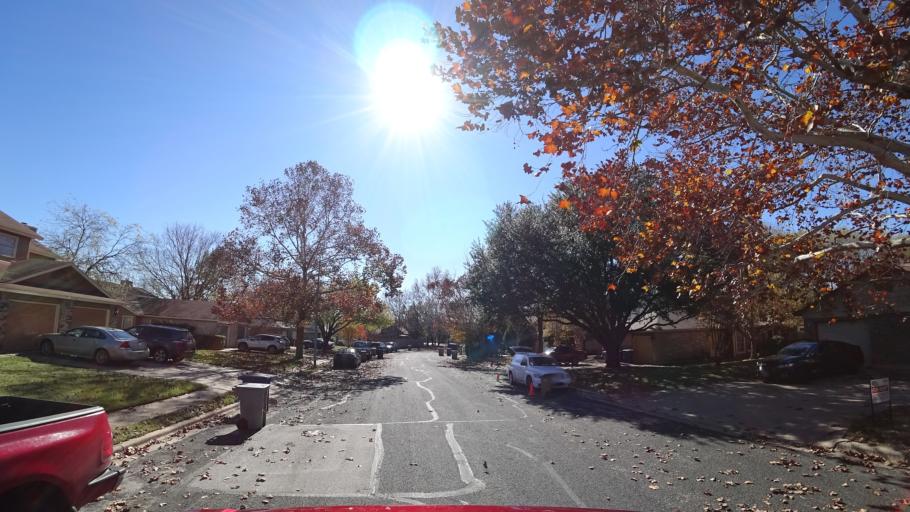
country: US
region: Texas
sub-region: Travis County
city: Wells Branch
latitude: 30.4108
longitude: -97.7010
